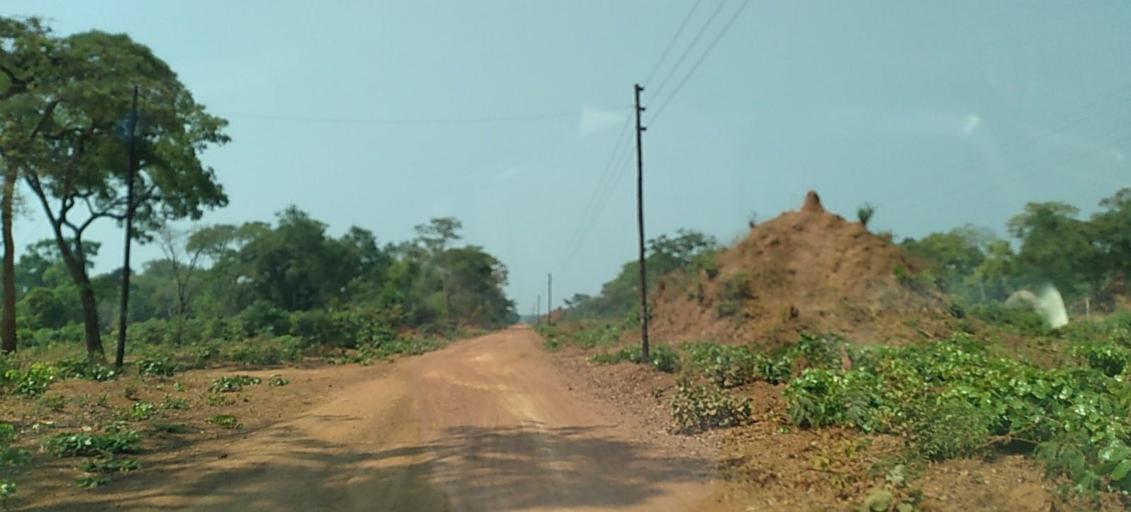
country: ZM
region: Copperbelt
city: Kalulushi
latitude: -13.0799
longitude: 27.4114
